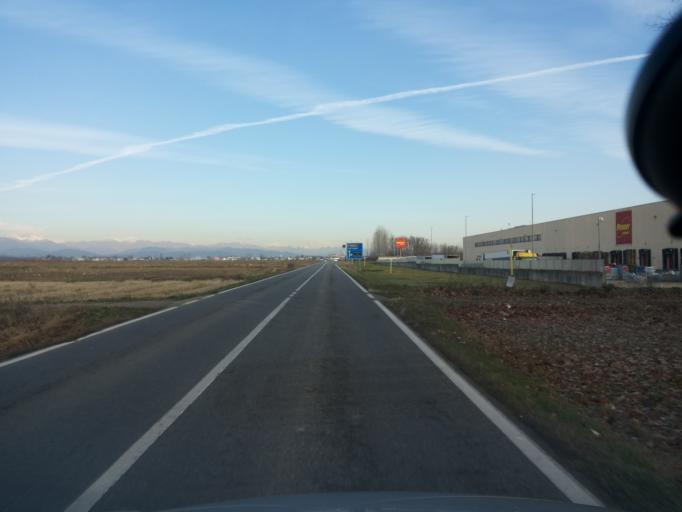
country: IT
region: Piedmont
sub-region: Provincia di Vercelli
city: Greggio
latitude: 45.4734
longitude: 8.3872
